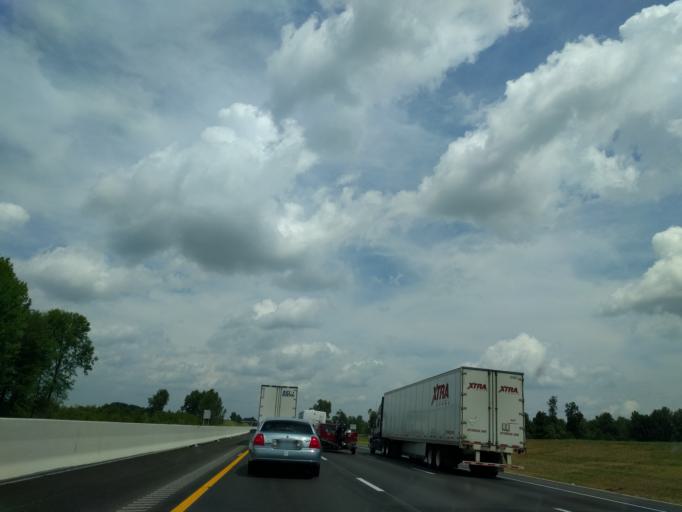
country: US
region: Kentucky
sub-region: Larue County
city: Hodgenville
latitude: 37.5314
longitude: -85.8827
